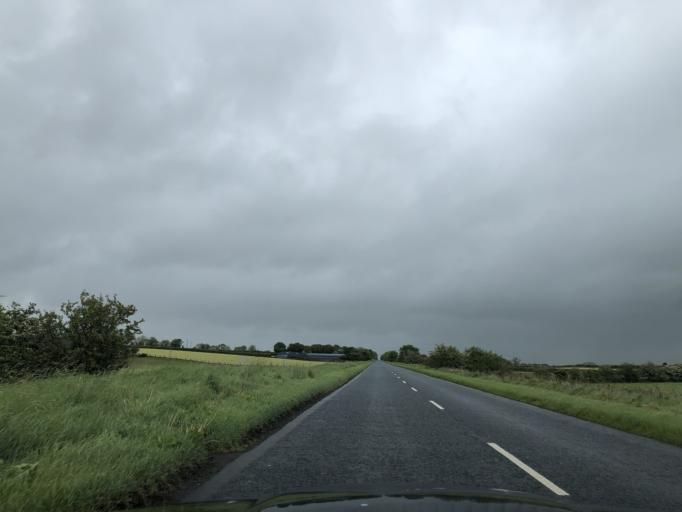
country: GB
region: Northern Ireland
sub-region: Moyle District
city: Ballycastle
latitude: 55.1735
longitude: -6.3400
